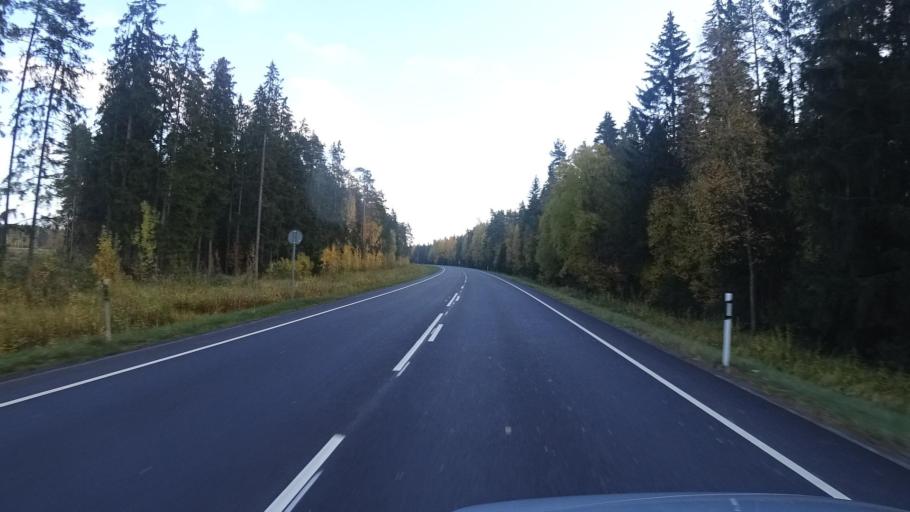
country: FI
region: Satakunta
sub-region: Rauma
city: Koeylioe
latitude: 61.0945
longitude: 22.2398
